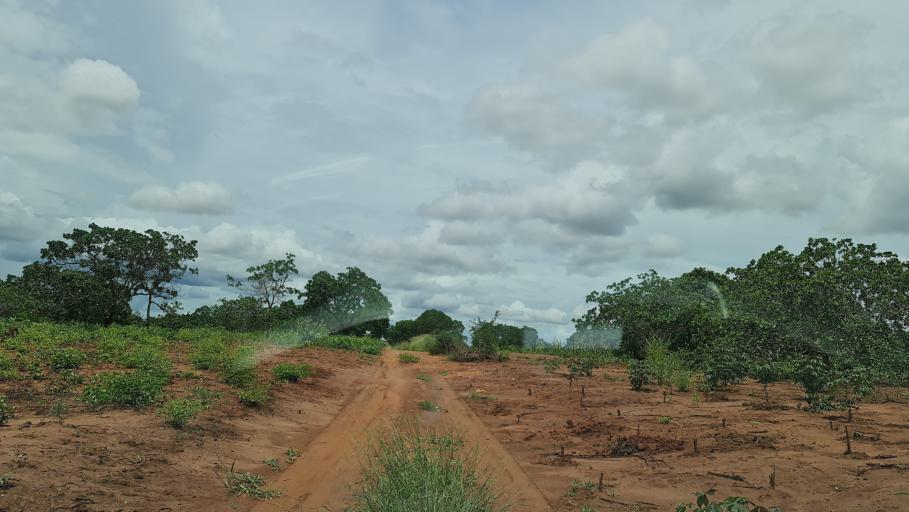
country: MZ
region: Nampula
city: Nacala
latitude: -14.7870
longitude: 39.9763
